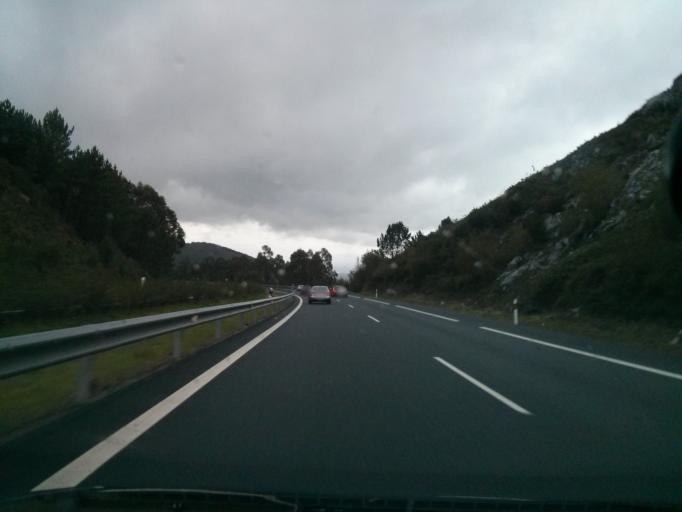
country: ES
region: Galicia
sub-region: Provincia de Pontevedra
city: Covelo
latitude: 42.1610
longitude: -8.3966
